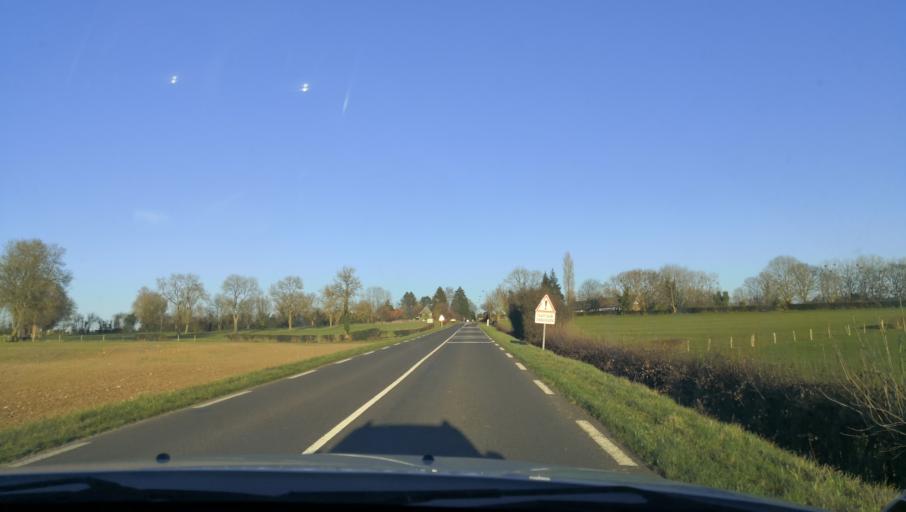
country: FR
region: Haute-Normandie
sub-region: Departement de la Seine-Maritime
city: Buchy
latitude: 49.5908
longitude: 1.4003
